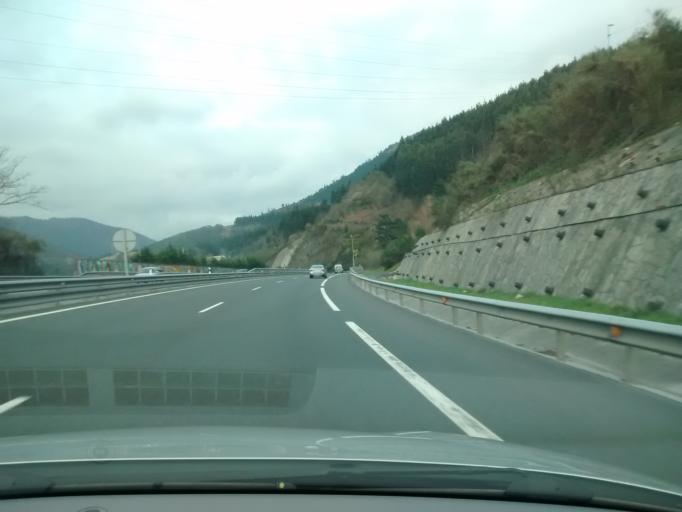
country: ES
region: Basque Country
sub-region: Bizkaia
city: Alonsotegi
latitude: 43.2200
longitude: -3.0225
